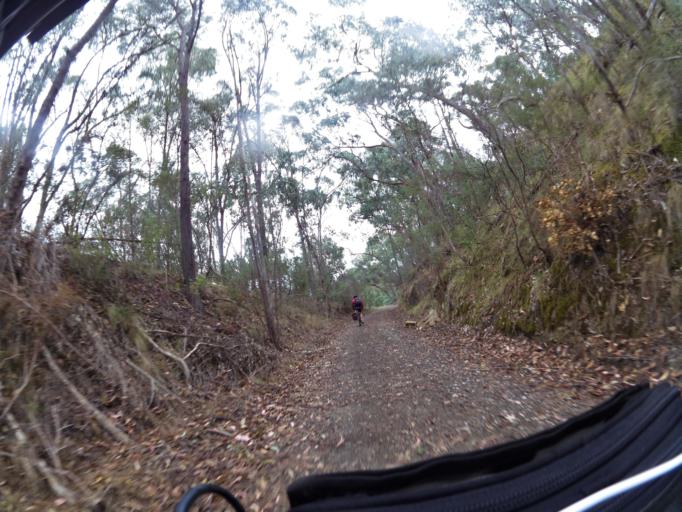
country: AU
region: New South Wales
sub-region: Greater Hume Shire
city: Holbrook
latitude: -36.1700
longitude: 147.4061
